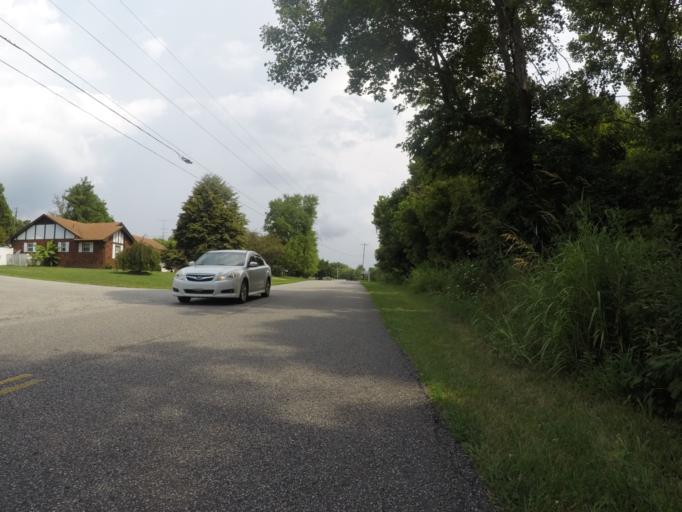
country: US
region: Kentucky
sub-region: Boyd County
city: Ironville
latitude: 38.4380
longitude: -82.7080
